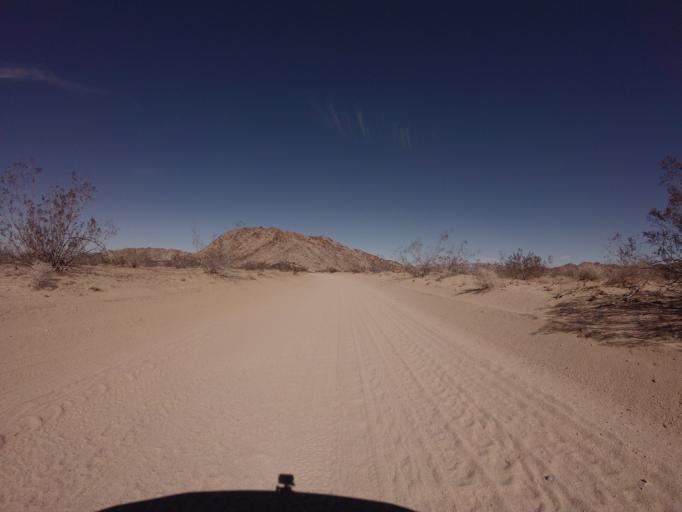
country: US
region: California
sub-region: San Bernardino County
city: Joshua Tree
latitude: 34.3106
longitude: -116.3970
